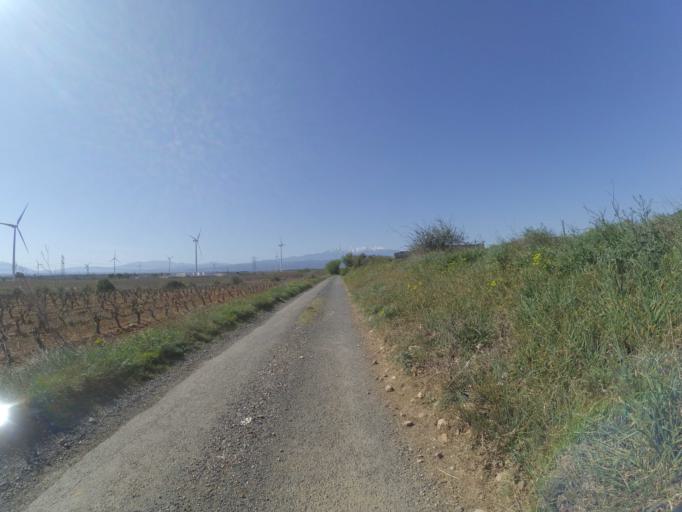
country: FR
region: Languedoc-Roussillon
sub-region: Departement des Pyrenees-Orientales
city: Baixas
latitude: 42.7326
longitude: 2.7771
